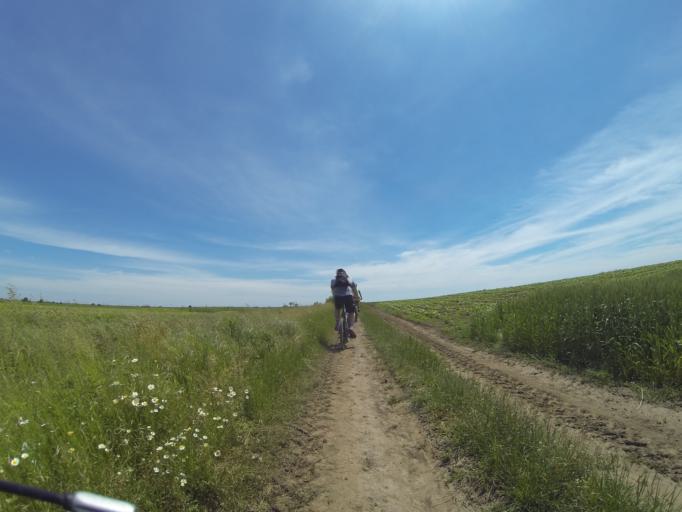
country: RO
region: Dolj
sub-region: Comuna Leu
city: Zanoaga
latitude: 44.1861
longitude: 24.0579
